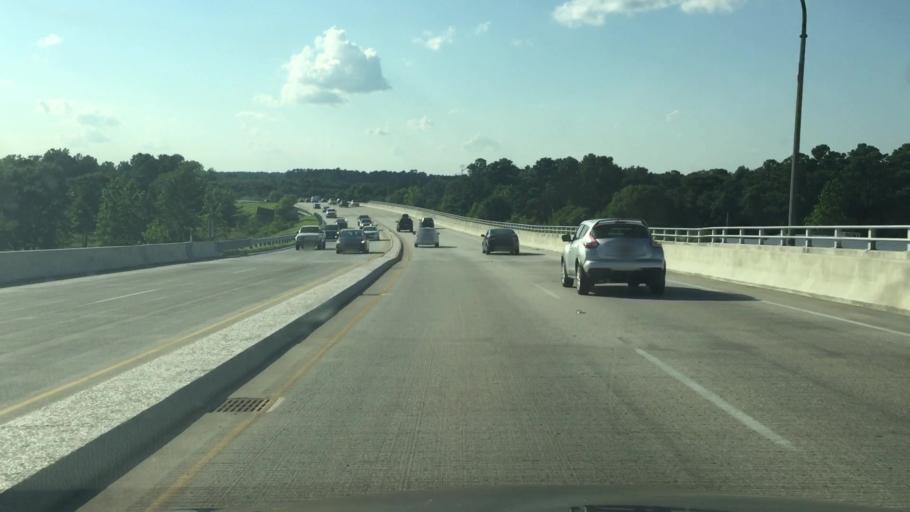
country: US
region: South Carolina
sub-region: Horry County
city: North Myrtle Beach
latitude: 33.8348
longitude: -78.6850
